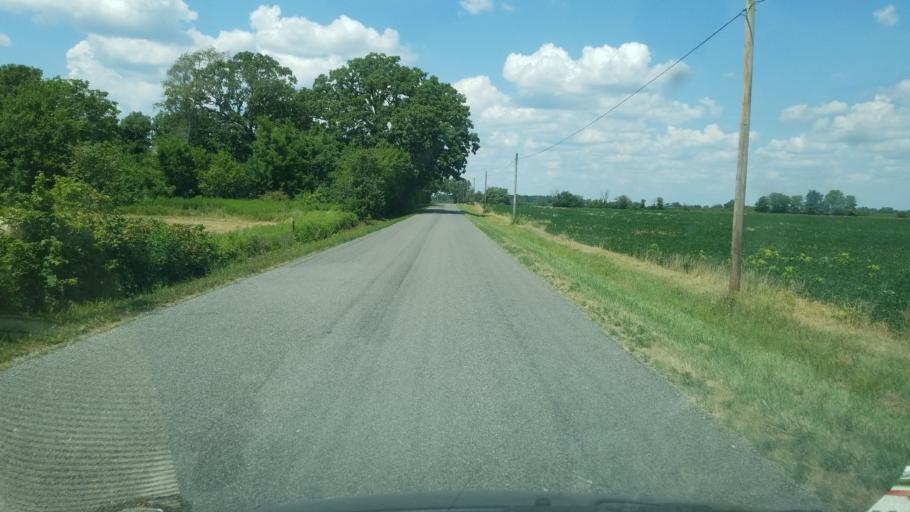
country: US
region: Ohio
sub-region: Champaign County
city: Mechanicsburg
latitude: 40.1031
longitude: -83.4681
